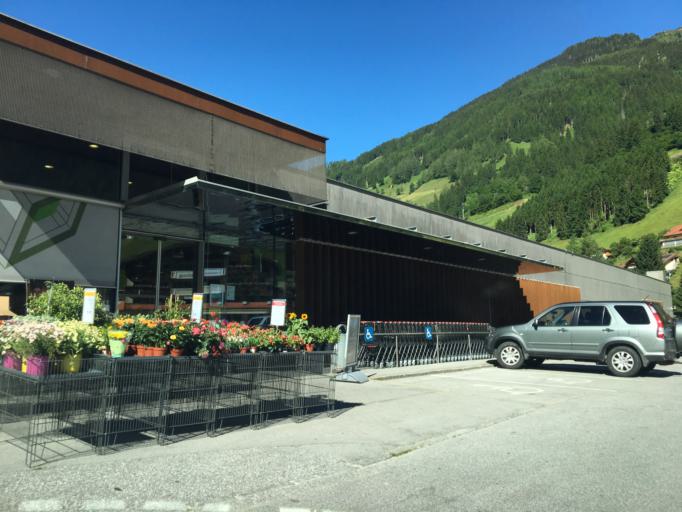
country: AT
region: Tyrol
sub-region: Politischer Bezirk Innsbruck Land
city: Neustift im Stubaital
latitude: 47.1123
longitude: 11.3100
